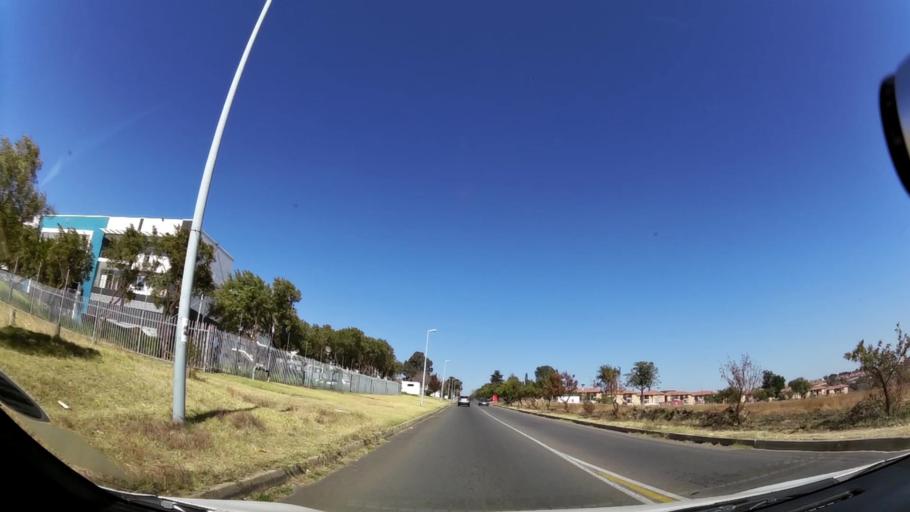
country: ZA
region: Gauteng
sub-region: City of Johannesburg Metropolitan Municipality
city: Midrand
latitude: -25.9655
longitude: 28.1274
